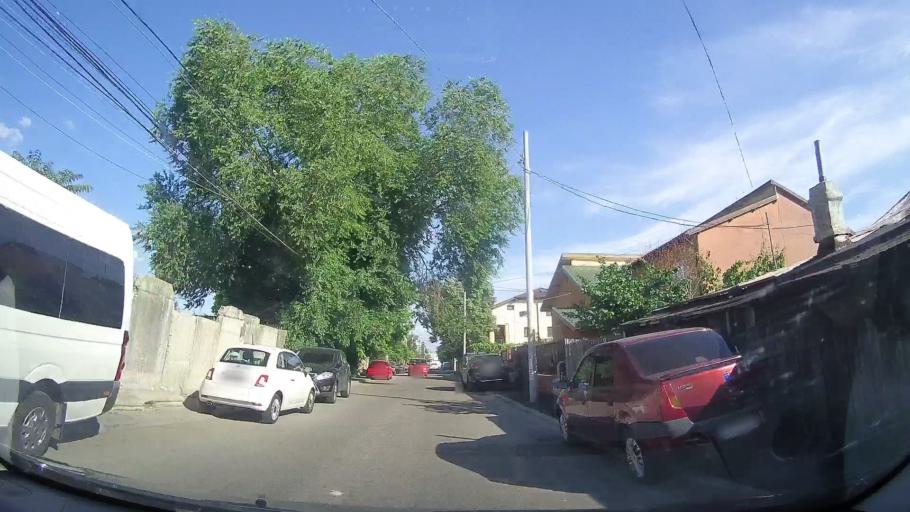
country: RO
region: Bucuresti
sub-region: Municipiul Bucuresti
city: Bucharest
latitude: 44.4096
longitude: 26.1332
